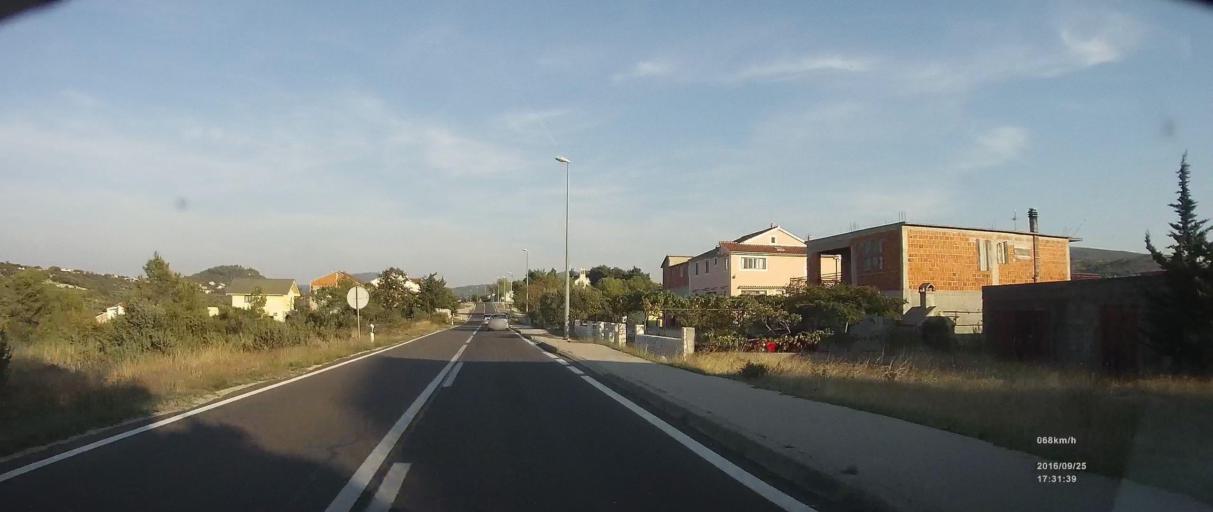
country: HR
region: Sibensko-Kniniska
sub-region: Grad Sibenik
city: Brodarica
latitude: 43.6772
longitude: 15.9921
